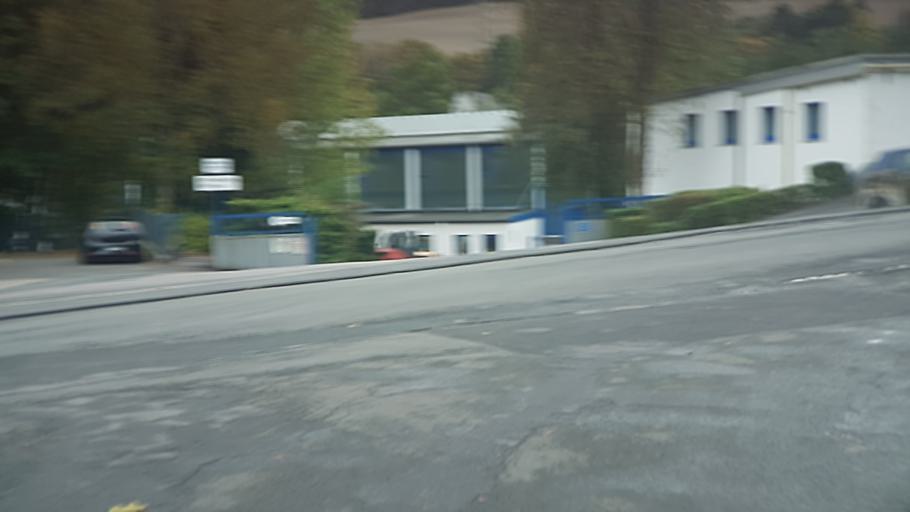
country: DE
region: North Rhine-Westphalia
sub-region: Regierungsbezirk Arnsberg
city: Herscheid
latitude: 51.2202
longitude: 7.6930
